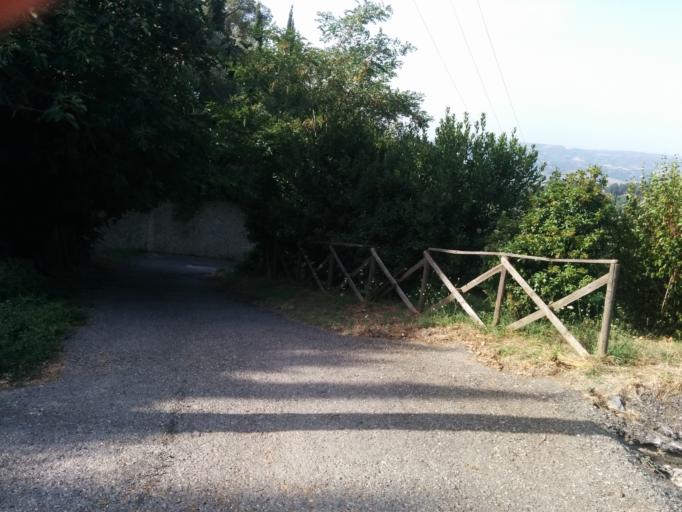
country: IT
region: Umbria
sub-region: Provincia di Terni
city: Sferracavallo
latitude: 42.7104
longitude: 12.0594
